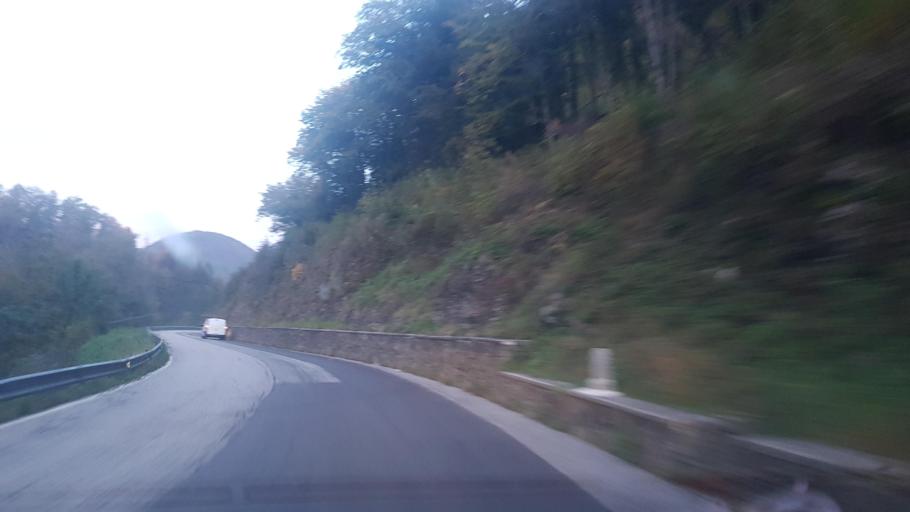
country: IT
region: Friuli Venezia Giulia
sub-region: Provincia di Udine
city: Chiaulis
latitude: 46.3868
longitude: 12.9989
